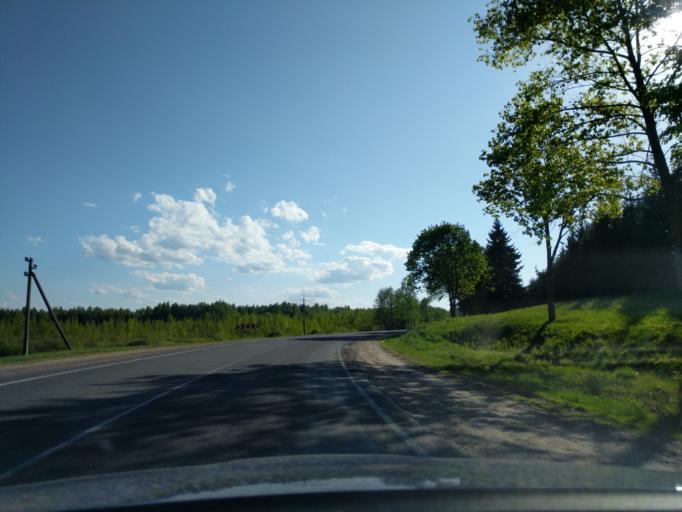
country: BY
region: Minsk
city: Myadzyel
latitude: 54.8603
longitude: 26.9316
